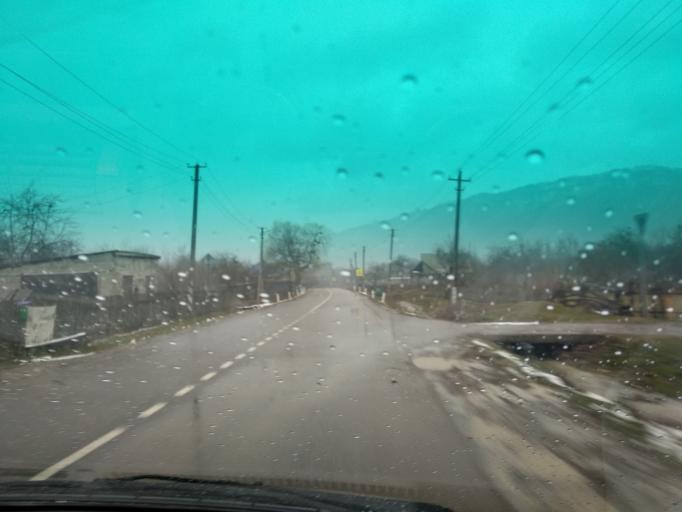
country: RU
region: Krasnodarskiy
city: Khadyzhensk
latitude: 44.2545
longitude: 39.3668
